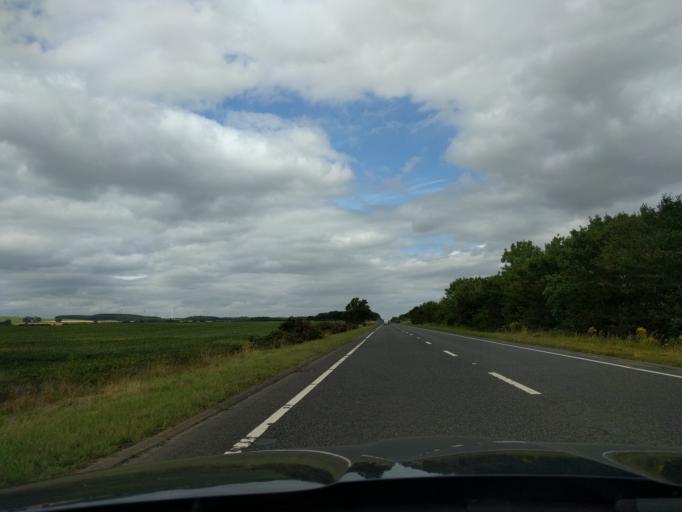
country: GB
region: England
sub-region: Northumberland
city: Ellingham
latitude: 55.4675
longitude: -1.7141
